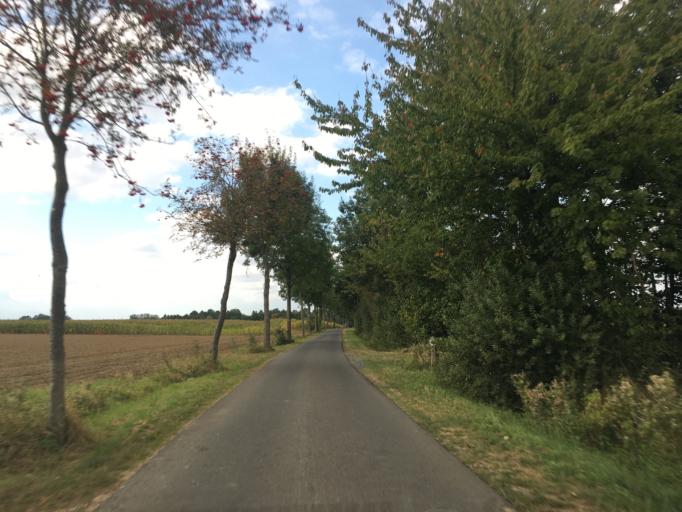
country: DE
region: North Rhine-Westphalia
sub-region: Regierungsbezirk Munster
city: Muenster
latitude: 51.9771
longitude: 7.5319
